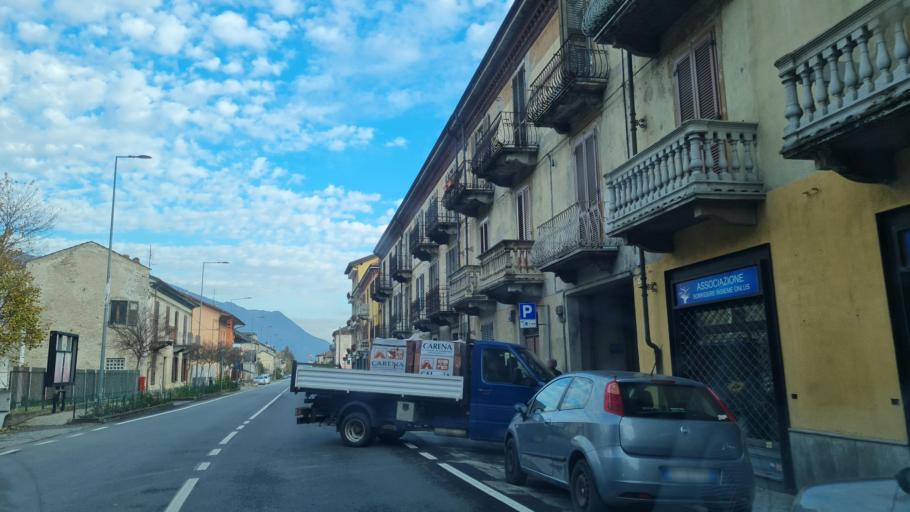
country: IT
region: Piedmont
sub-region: Provincia di Torino
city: Bussoleno
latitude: 45.1385
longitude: 7.1523
